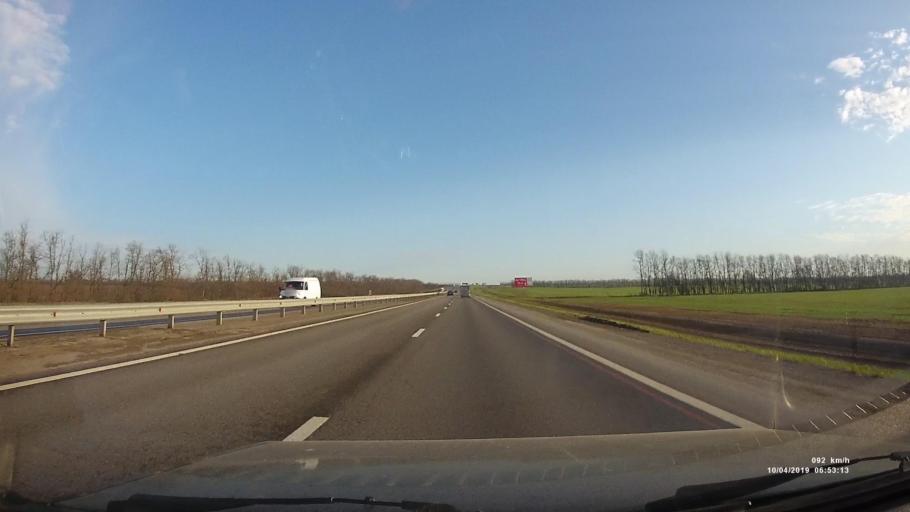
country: RU
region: Rostov
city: Grushevskaya
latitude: 47.4759
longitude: 39.9703
